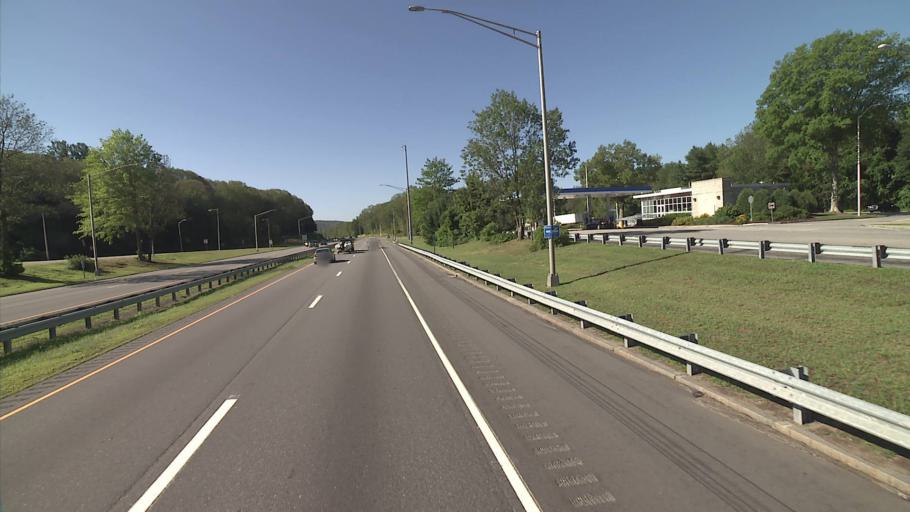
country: US
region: Connecticut
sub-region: New London County
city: Oxoboxo River
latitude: 41.4738
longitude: -72.1167
